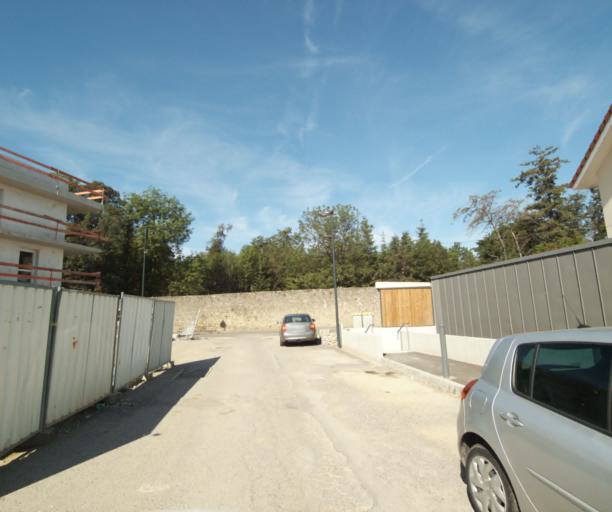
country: FR
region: Rhone-Alpes
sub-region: Departement de la Haute-Savoie
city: Marin
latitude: 46.3934
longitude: 6.5034
